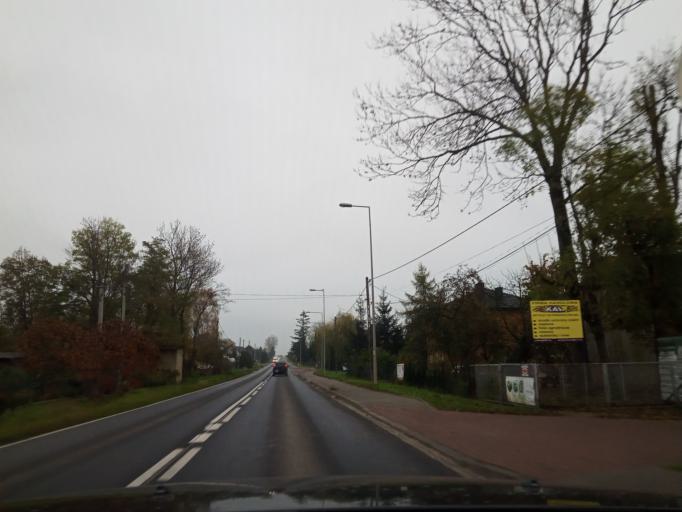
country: PL
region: Lesser Poland Voivodeship
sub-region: Powiat proszowicki
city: Proszowice
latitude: 50.1790
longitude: 20.2558
